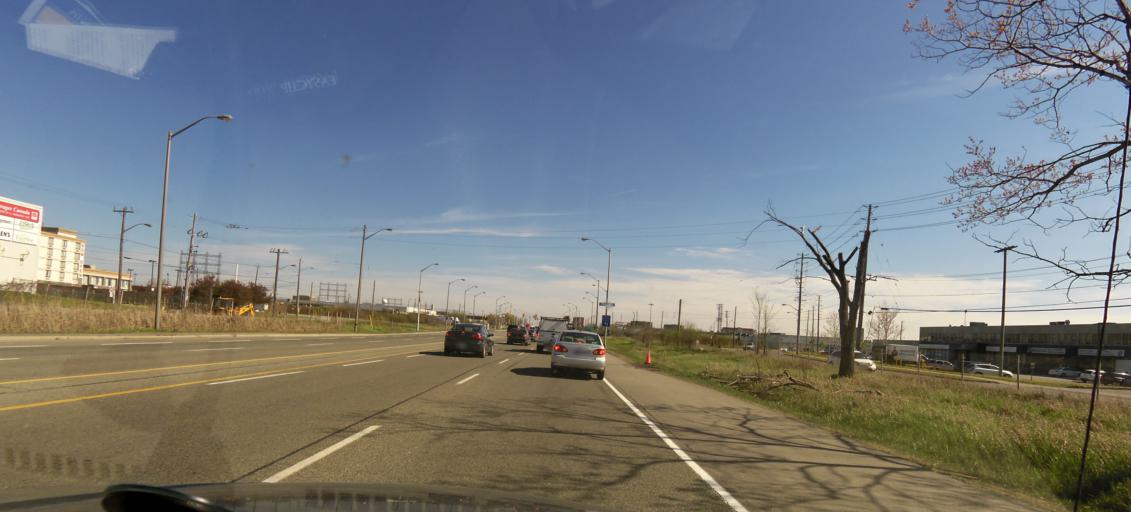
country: CA
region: Ontario
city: Etobicoke
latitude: 43.7012
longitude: -79.5881
